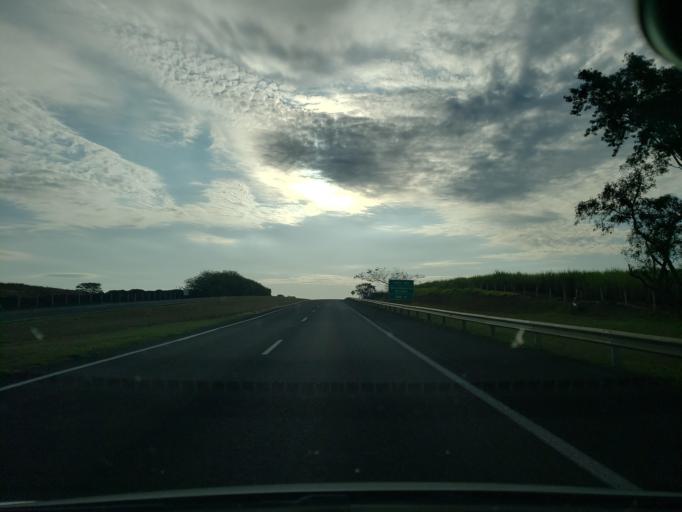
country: BR
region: Sao Paulo
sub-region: Mirandopolis
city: Mirandopolis
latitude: -21.0913
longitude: -51.0545
